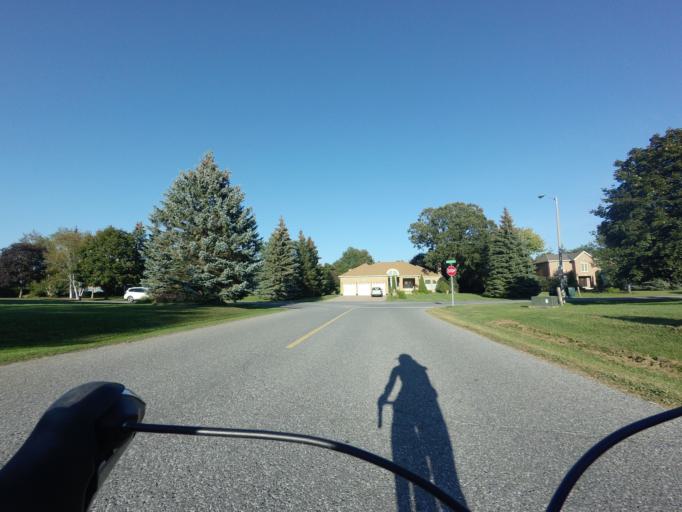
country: CA
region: Ontario
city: Bells Corners
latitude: 45.2186
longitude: -75.6970
